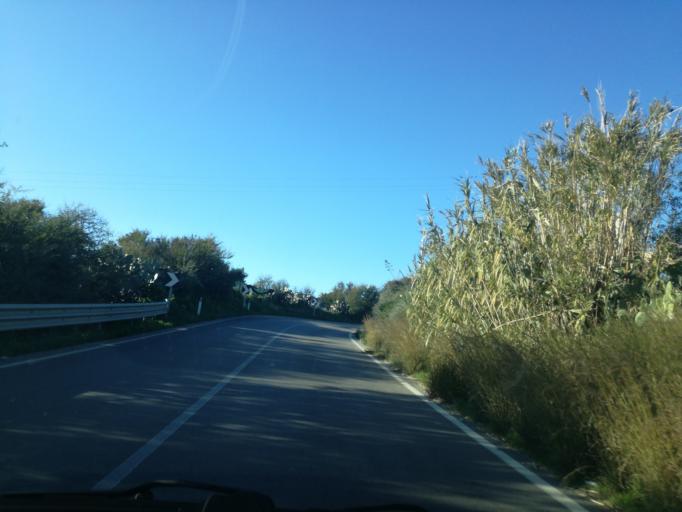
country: IT
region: Sicily
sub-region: Provincia di Caltanissetta
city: Gela
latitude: 37.1080
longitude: 14.1608
